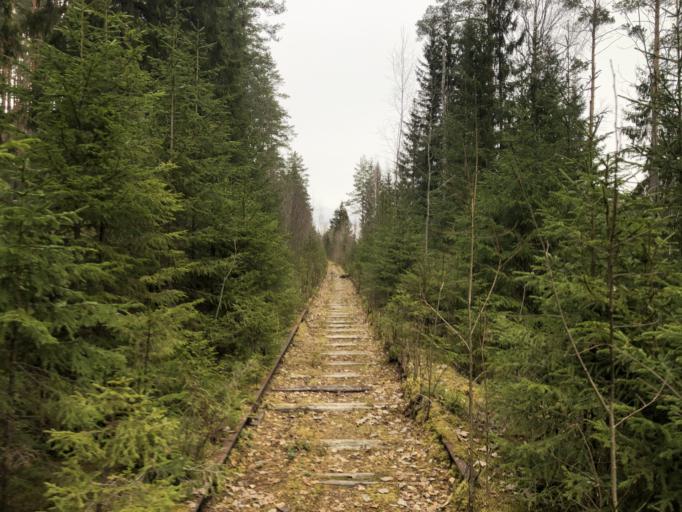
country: SE
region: Vaermland
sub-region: Filipstads Kommun
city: Lesjofors
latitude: 59.9650
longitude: 14.1938
